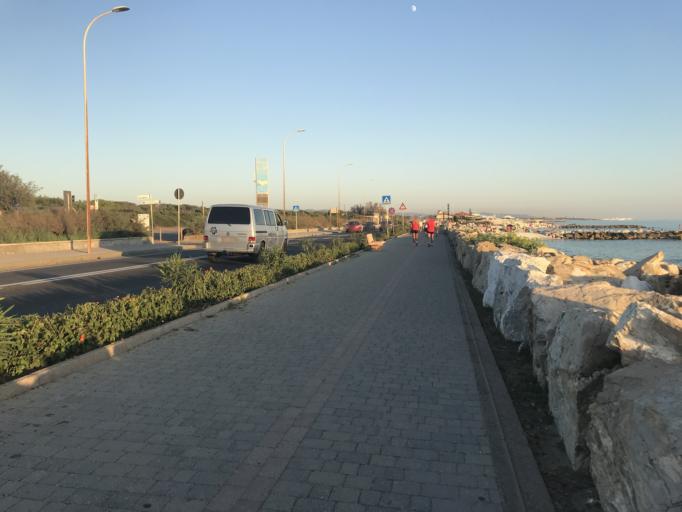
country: IT
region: Tuscany
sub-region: Province of Pisa
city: Marina di Pisa
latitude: 43.6586
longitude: 10.2802
